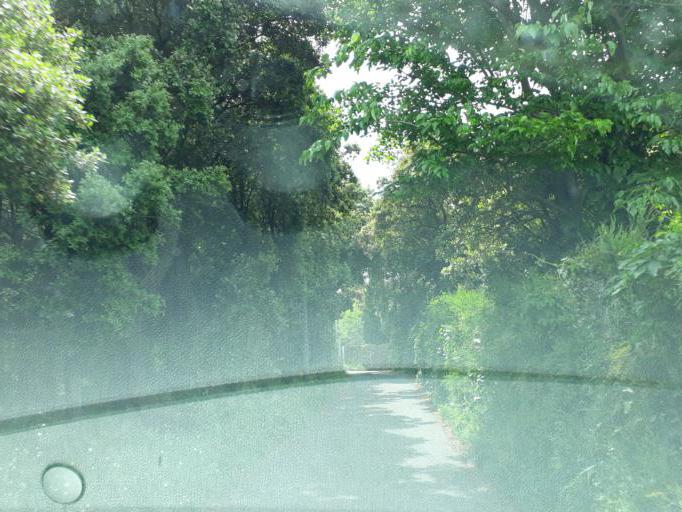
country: FR
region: Languedoc-Roussillon
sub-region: Departement de l'Herault
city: Agde
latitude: 43.2935
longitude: 3.4903
